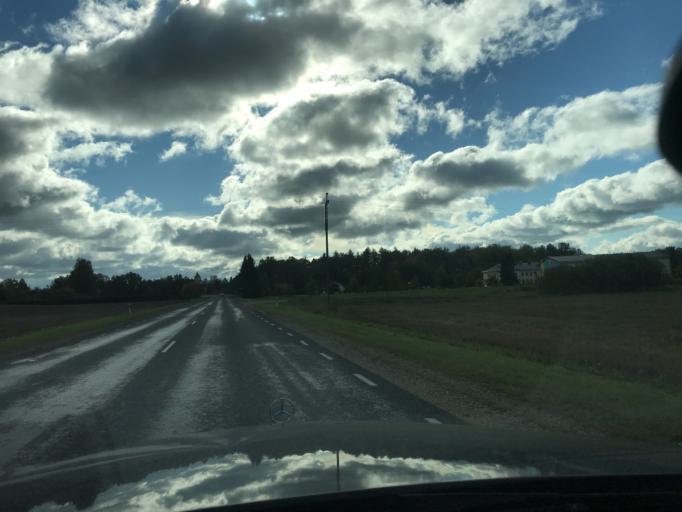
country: EE
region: Vorumaa
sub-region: Antsla vald
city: Vana-Antsla
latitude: 57.9598
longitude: 26.2730
